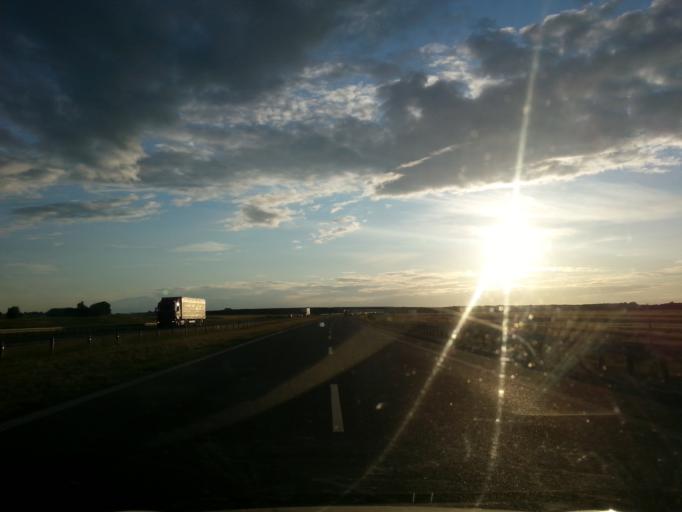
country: PL
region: Lodz Voivodeship
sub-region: Powiat wieruszowski
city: Sokolniki
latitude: 51.3186
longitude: 18.3574
